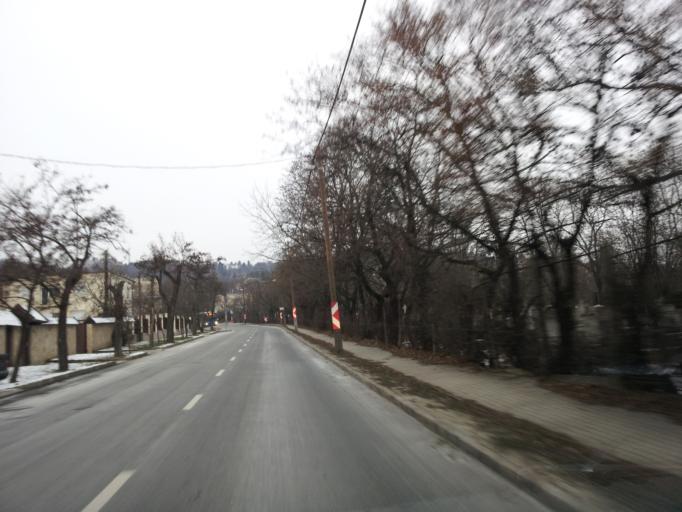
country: HU
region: Budapest
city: Budapest XII. keruelet
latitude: 47.4855
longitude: 18.9937
